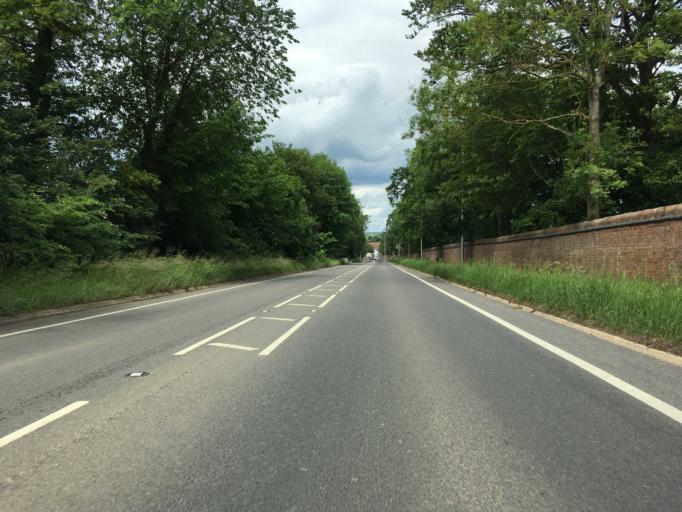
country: GB
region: England
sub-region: Northamptonshire
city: Towcester
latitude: 52.1256
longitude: -0.9786
